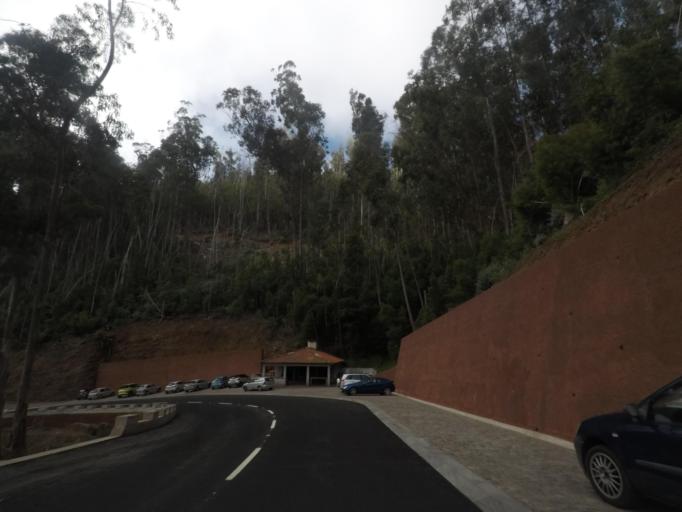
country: PT
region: Madeira
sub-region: Calheta
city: Arco da Calheta
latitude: 32.7538
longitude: -17.1492
